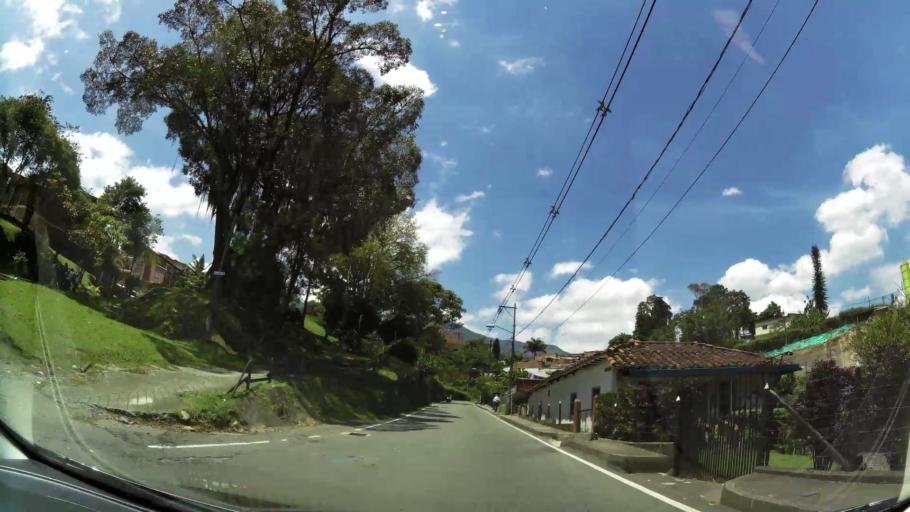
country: CO
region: Antioquia
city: La Estrella
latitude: 6.1854
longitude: -75.6452
